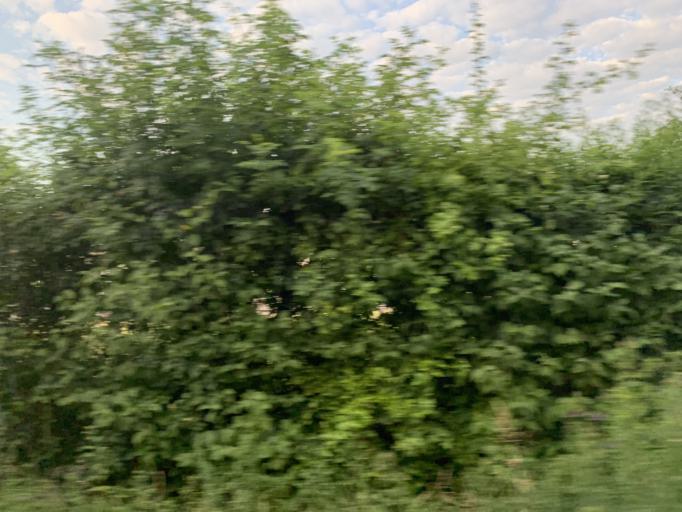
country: FR
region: Rhone-Alpes
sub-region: Departement du Rhone
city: Meyzieu
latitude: 45.7699
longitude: 5.0131
